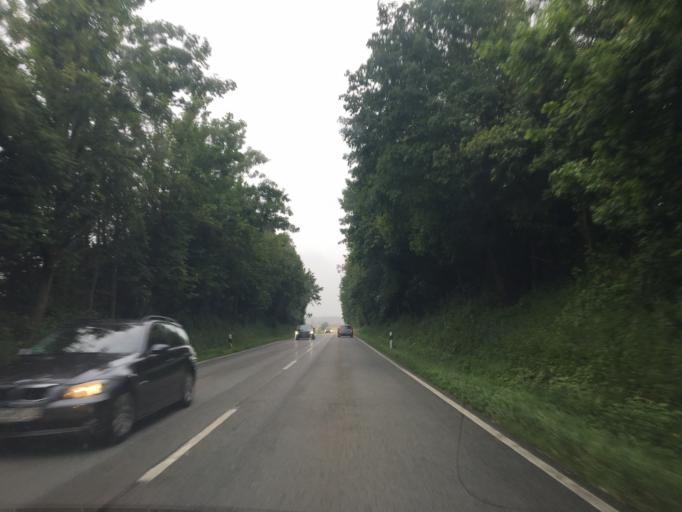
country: DE
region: Bavaria
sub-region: Upper Bavaria
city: Warngau
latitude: 47.8184
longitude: 11.7128
